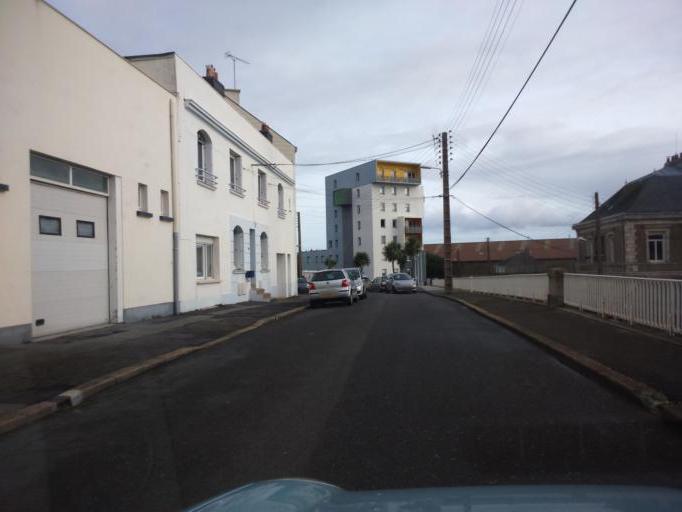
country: FR
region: Pays de la Loire
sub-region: Departement de la Loire-Atlantique
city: Saint-Nazaire
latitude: 47.2710
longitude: -2.2012
